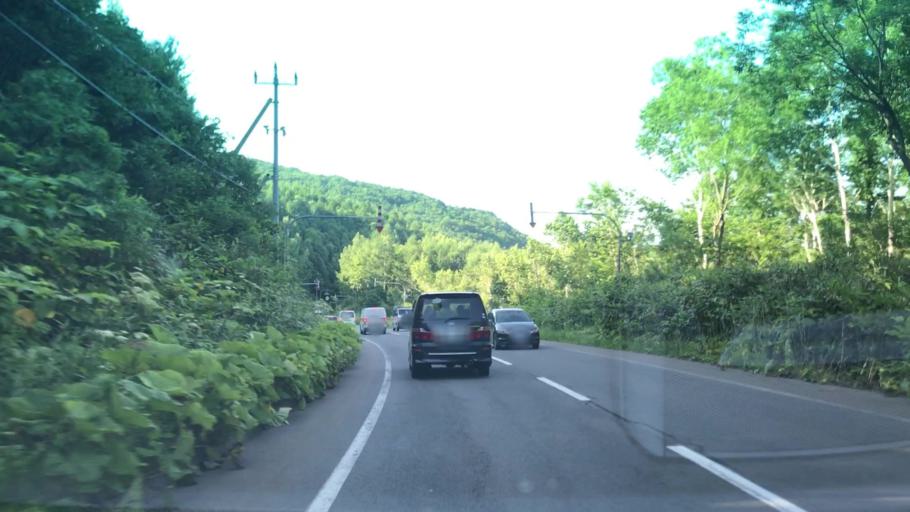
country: JP
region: Hokkaido
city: Otaru
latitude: 43.1144
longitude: 141.0096
